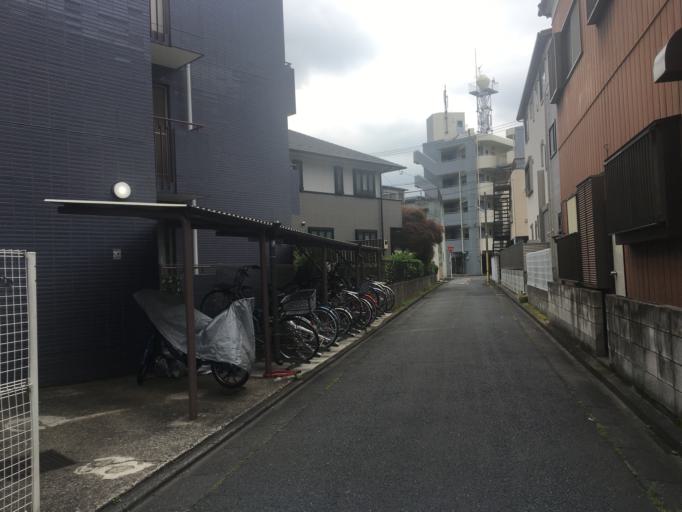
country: JP
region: Saitama
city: Kawaguchi
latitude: 35.8092
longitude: 139.7201
